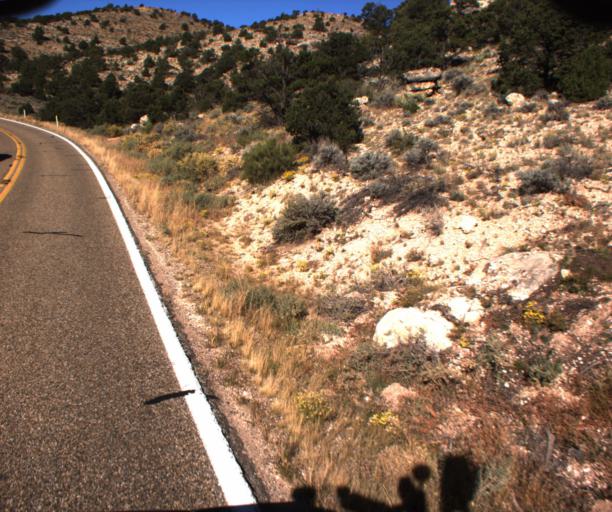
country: US
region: Arizona
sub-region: Coconino County
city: Fredonia
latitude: 36.7253
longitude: -112.0749
